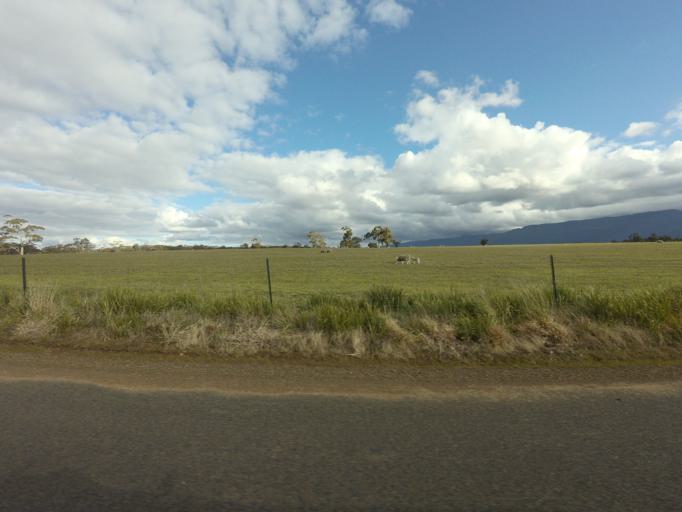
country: AU
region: Tasmania
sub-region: Northern Midlands
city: Evandale
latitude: -41.8652
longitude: 147.2701
